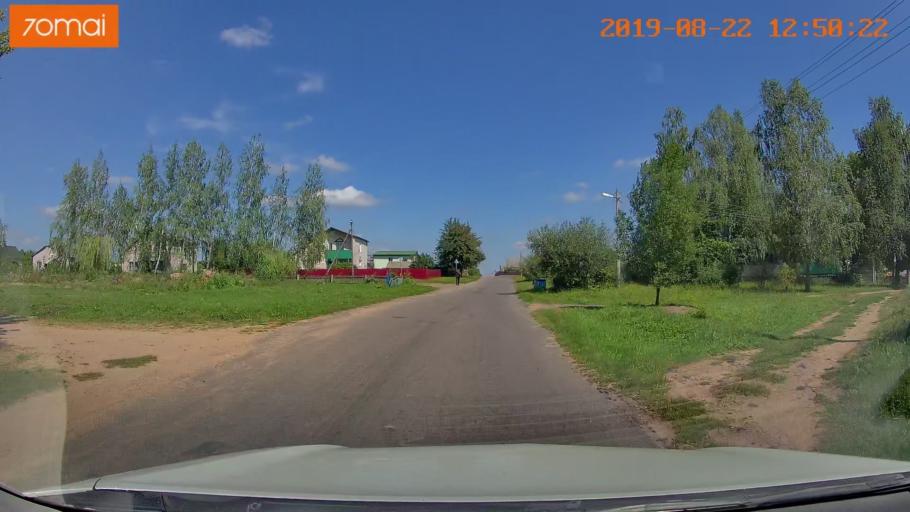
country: BY
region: Minsk
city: Prawdzinski
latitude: 53.4606
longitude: 27.6428
